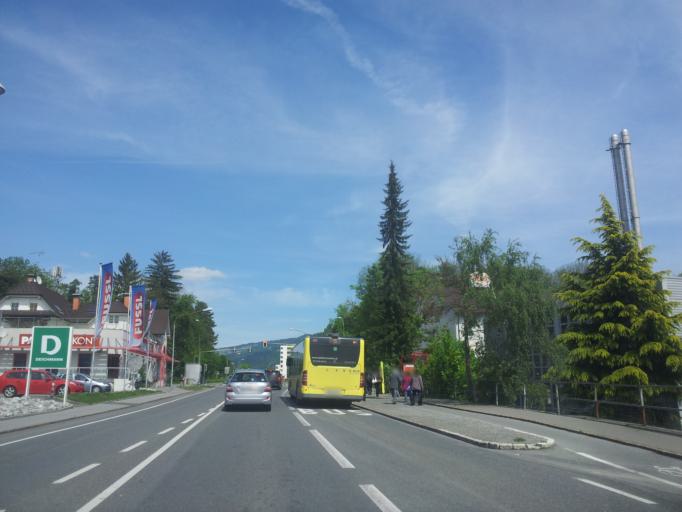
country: AT
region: Vorarlberg
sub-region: Politischer Bezirk Bregenz
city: Hard
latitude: 47.4907
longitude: 9.7062
